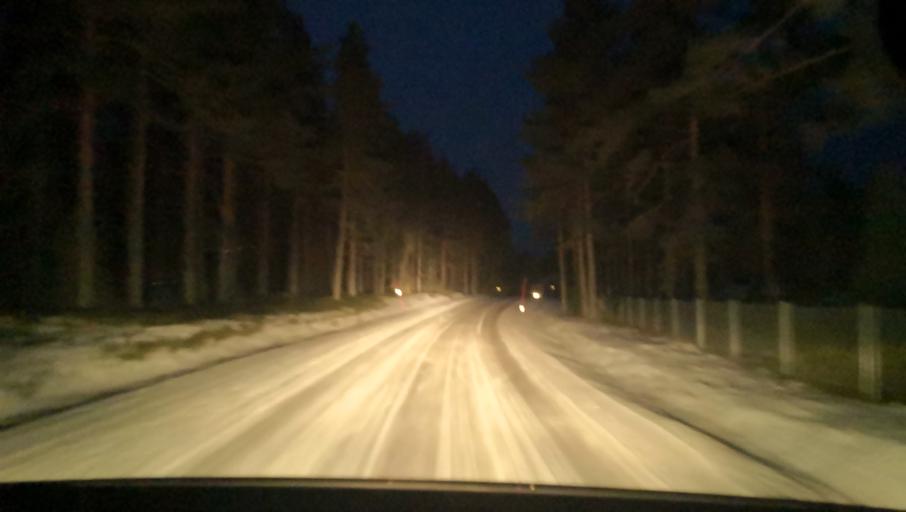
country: SE
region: Uppsala
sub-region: Heby Kommun
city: Tarnsjo
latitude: 60.2838
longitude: 16.8052
